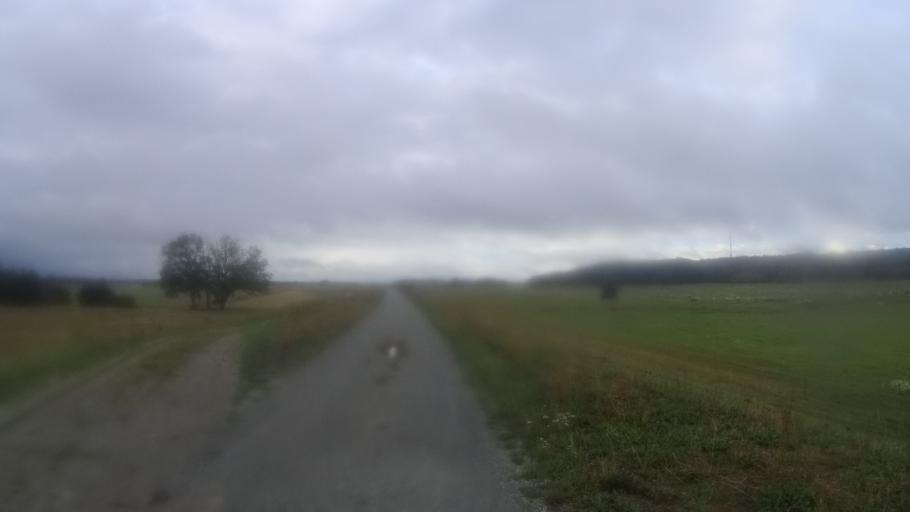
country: DE
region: Brandenburg
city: Lenzen
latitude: 53.0798
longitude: 11.4177
